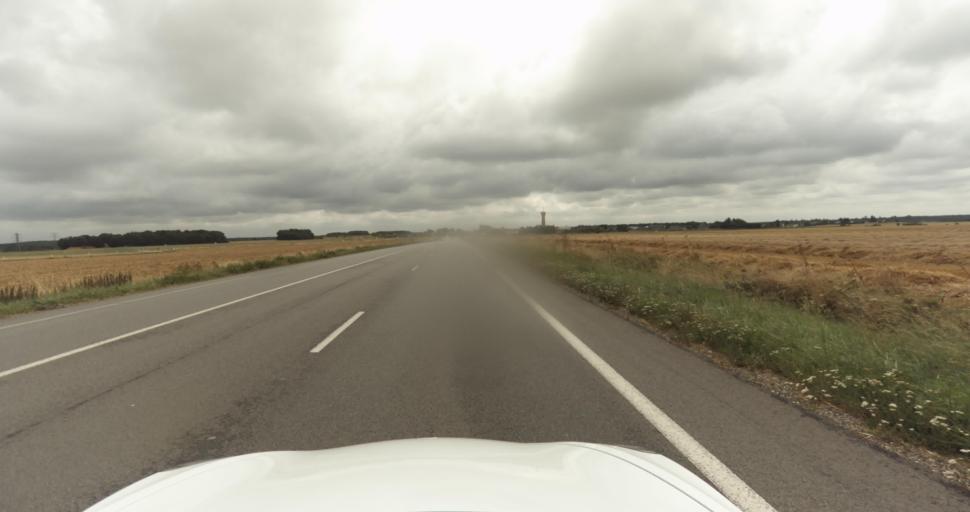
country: FR
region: Haute-Normandie
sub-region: Departement de l'Eure
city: Saint-Sebastien-de-Morsent
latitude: 49.0401
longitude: 1.0839
